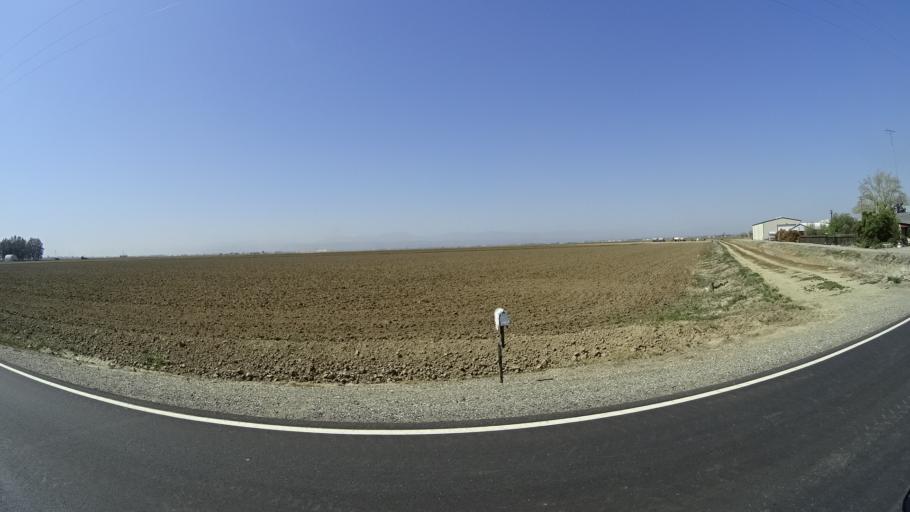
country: US
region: California
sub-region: Glenn County
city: Willows
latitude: 39.4790
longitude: -122.1366
